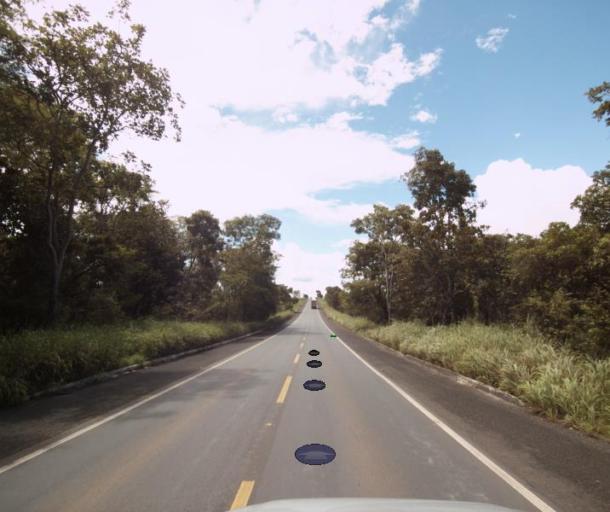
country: BR
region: Goias
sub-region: Uruacu
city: Uruacu
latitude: -14.1512
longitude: -49.1192
